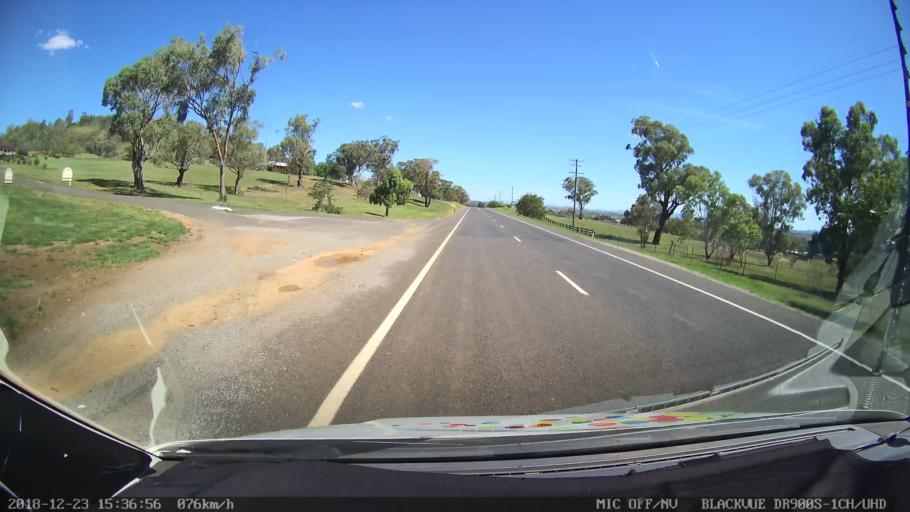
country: AU
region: New South Wales
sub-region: Tamworth Municipality
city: Tamworth
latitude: -31.0467
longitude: 150.8884
